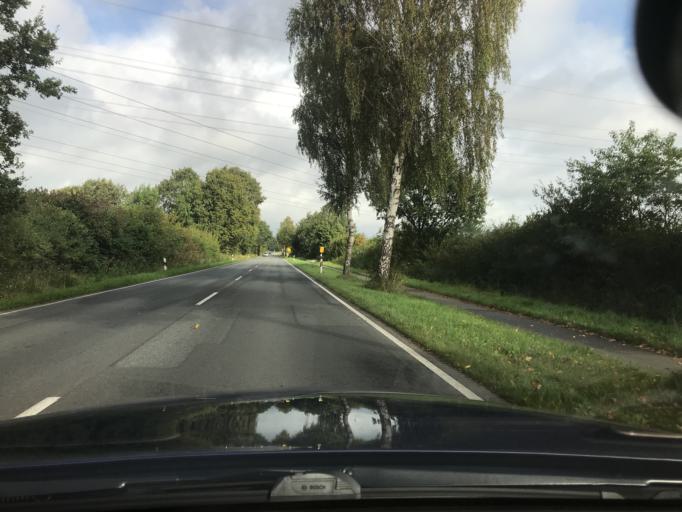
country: DE
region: Lower Saxony
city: Deinste
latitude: 53.5357
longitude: 9.4712
